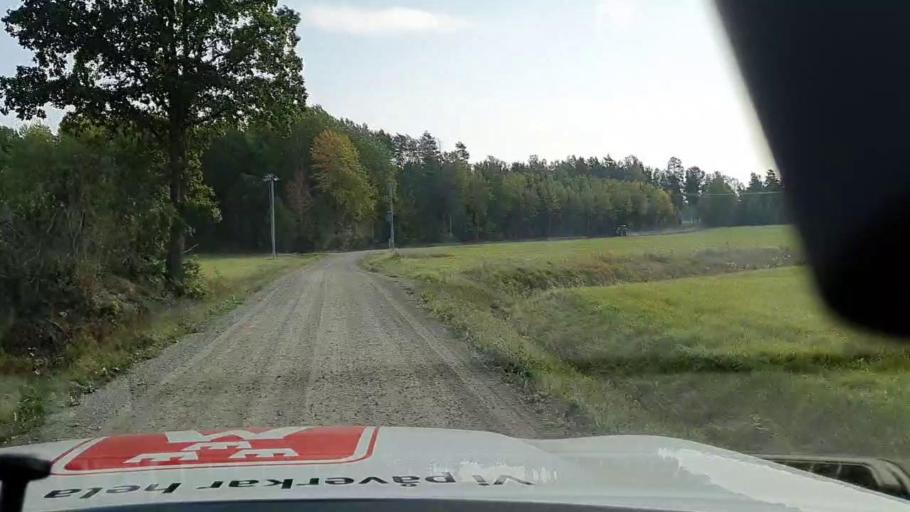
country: SE
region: Vaestmanland
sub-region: Kungsors Kommun
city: Kungsoer
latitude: 59.3599
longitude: 16.1458
